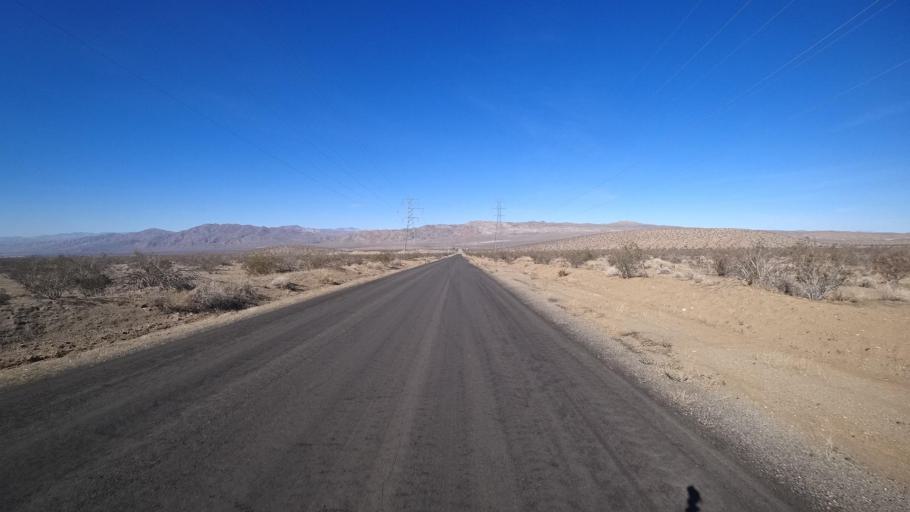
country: US
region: California
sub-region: Kern County
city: Ridgecrest
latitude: 35.3882
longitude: -117.6661
